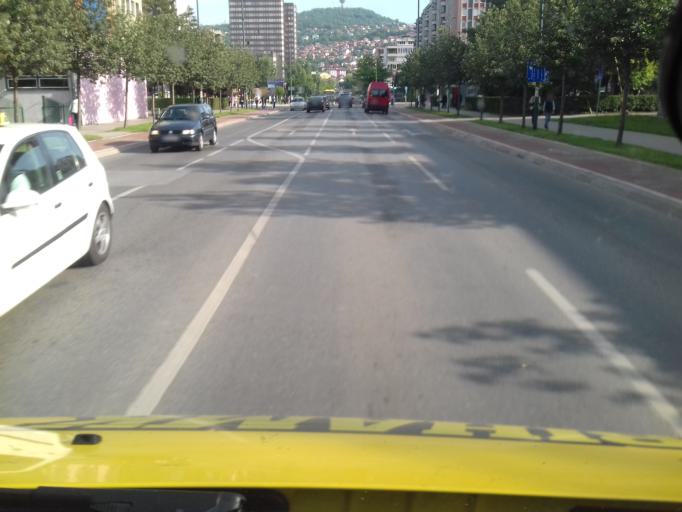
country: BA
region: Federation of Bosnia and Herzegovina
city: Kobilja Glava
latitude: 43.8532
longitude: 18.3929
